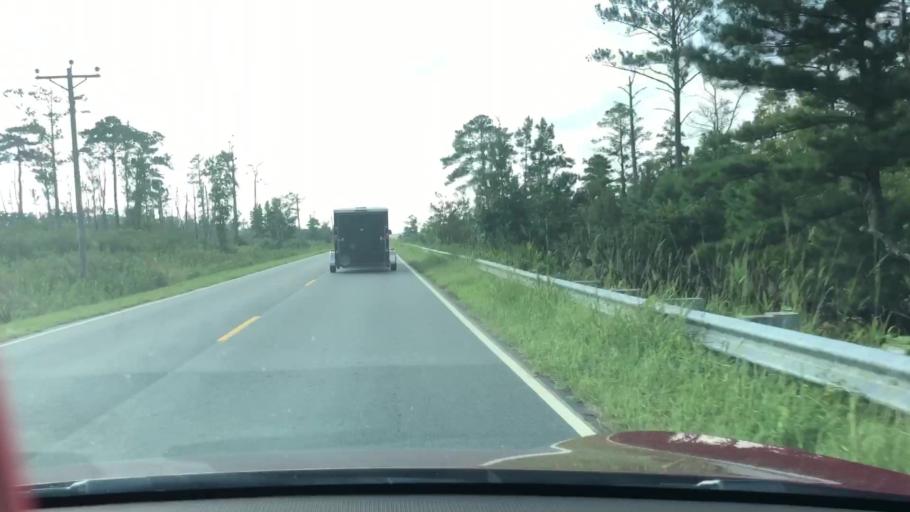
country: US
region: North Carolina
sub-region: Dare County
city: Wanchese
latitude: 35.6167
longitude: -75.8325
